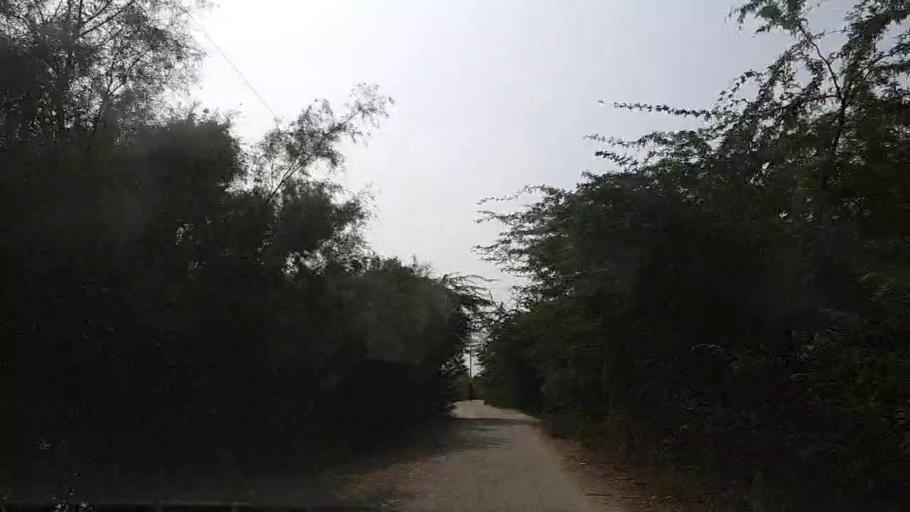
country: PK
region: Sindh
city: Mirpur Sakro
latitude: 24.6067
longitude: 67.7256
